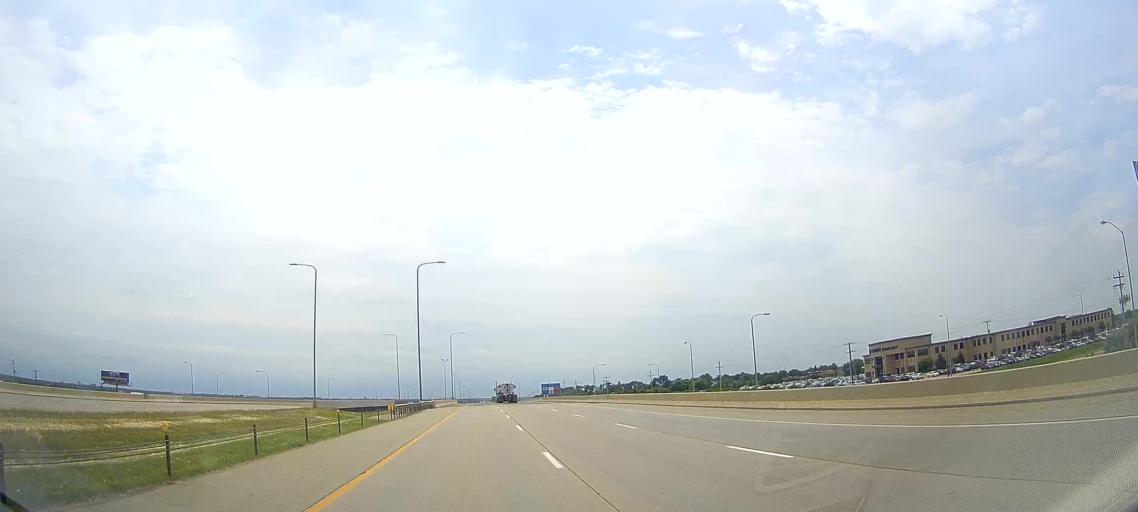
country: US
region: South Dakota
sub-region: Minnehaha County
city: Sioux Falls
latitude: 43.5882
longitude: -96.7713
